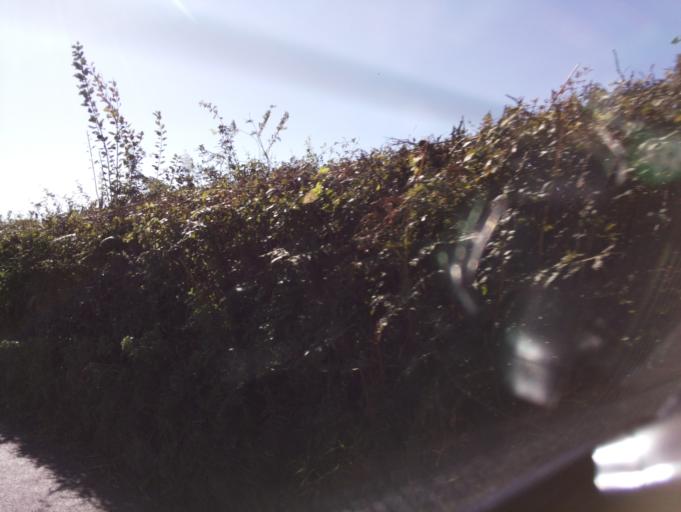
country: GB
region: Wales
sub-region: Torfaen County Borough
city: Cwmbran
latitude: 51.6275
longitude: -3.0508
